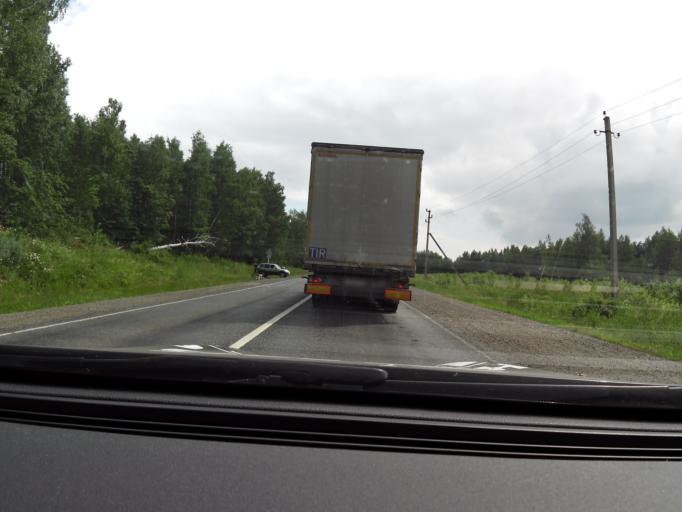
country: RU
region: Perm
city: Suksun
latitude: 57.0884
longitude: 57.3956
